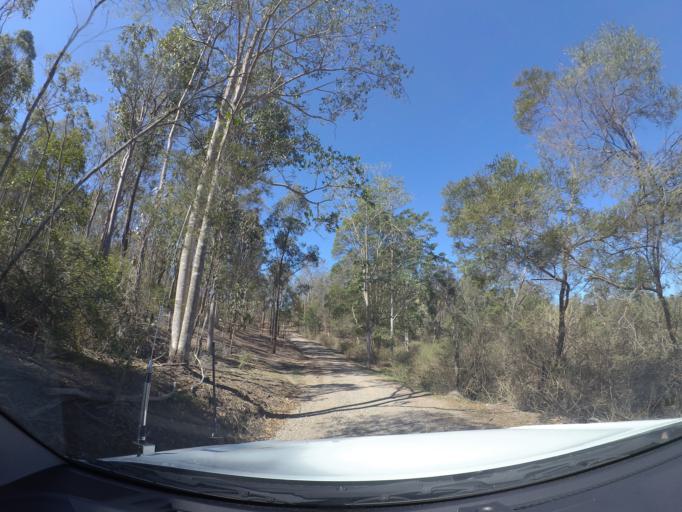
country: AU
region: Queensland
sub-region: Ipswich
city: Springfield Lakes
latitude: -27.7475
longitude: 152.8998
